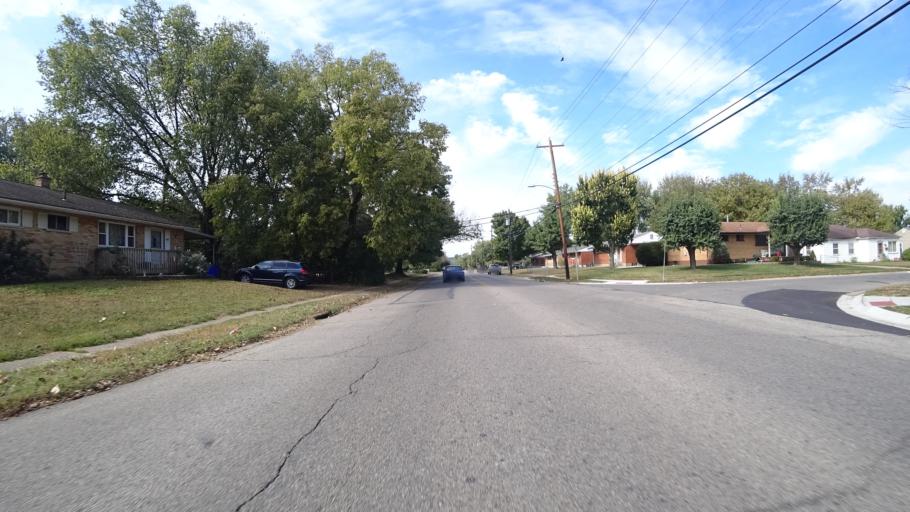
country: US
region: Ohio
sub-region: Butler County
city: Fairfield
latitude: 39.3587
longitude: -84.5489
